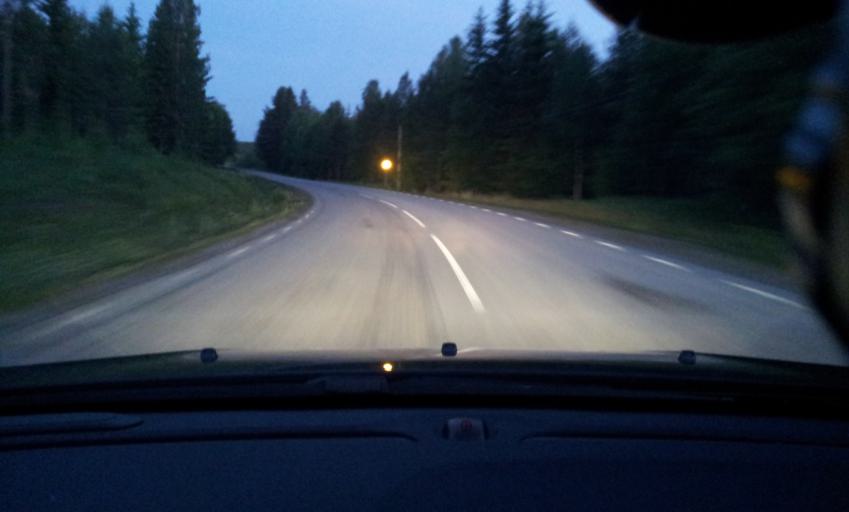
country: SE
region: Jaemtland
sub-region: OEstersunds Kommun
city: Brunflo
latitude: 62.7715
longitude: 14.9983
